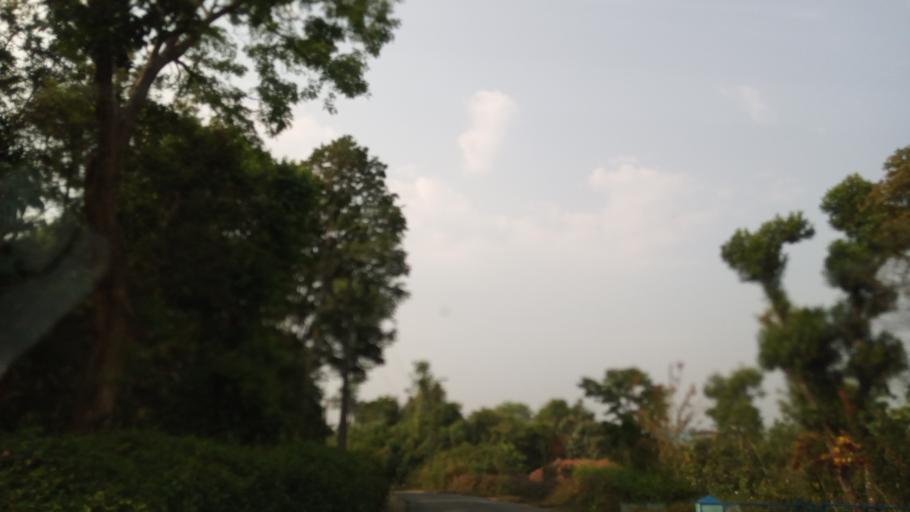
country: IN
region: Karnataka
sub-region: Chikmagalur
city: Mudigere
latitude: 13.0602
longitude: 75.6542
